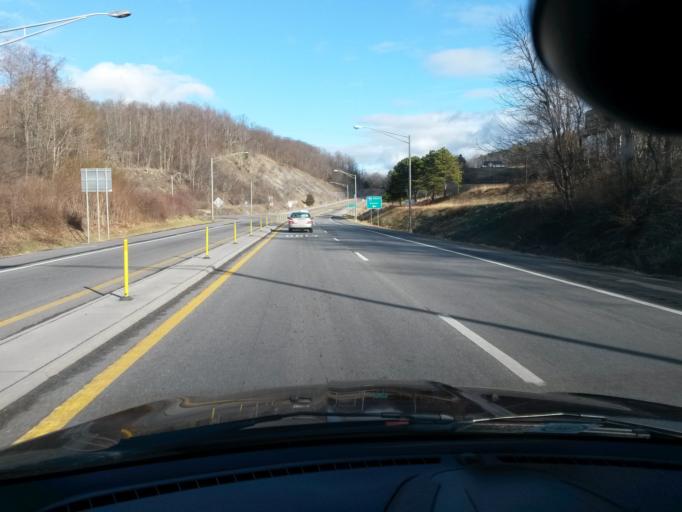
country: US
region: West Virginia
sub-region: Mercer County
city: Princeton
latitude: 37.2848
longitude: -81.1250
